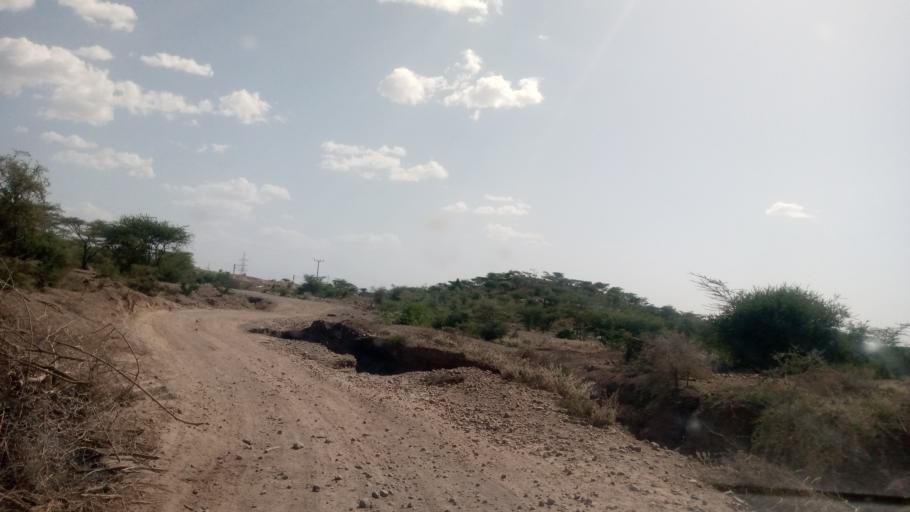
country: ET
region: Oromiya
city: Hirna
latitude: 9.5494
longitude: 41.1633
